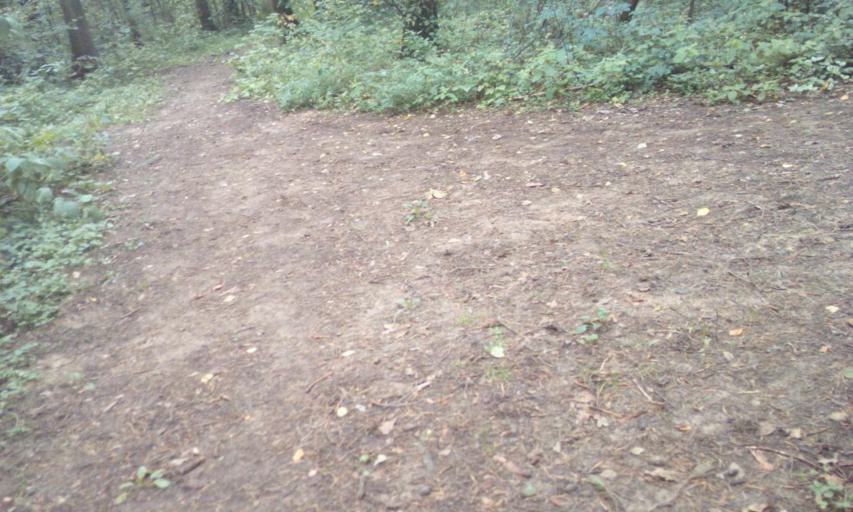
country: RU
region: Moskovskaya
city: Zhavoronki
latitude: 55.6635
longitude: 37.1250
